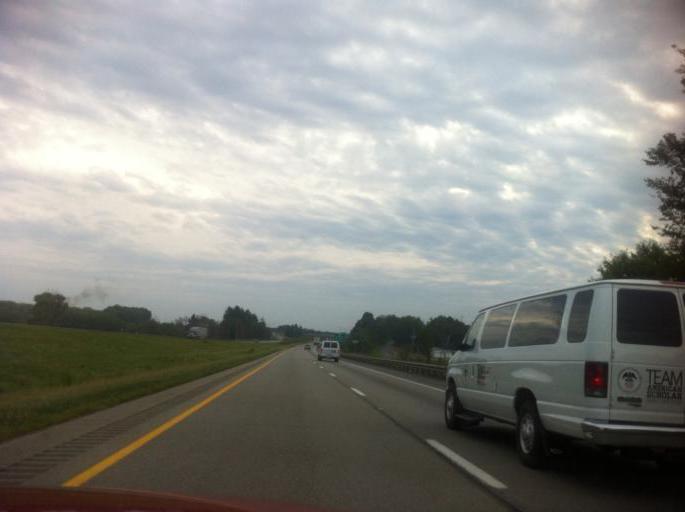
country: US
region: Pennsylvania
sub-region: Mercer County
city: Grove City
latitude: 41.2022
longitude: -79.9640
